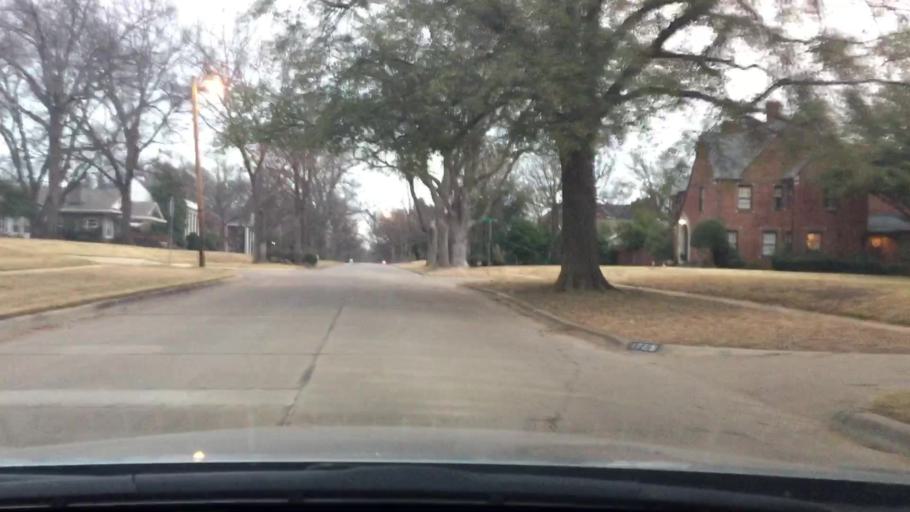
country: US
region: Oklahoma
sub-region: Carter County
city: Ardmore
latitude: 34.1720
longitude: -97.1498
